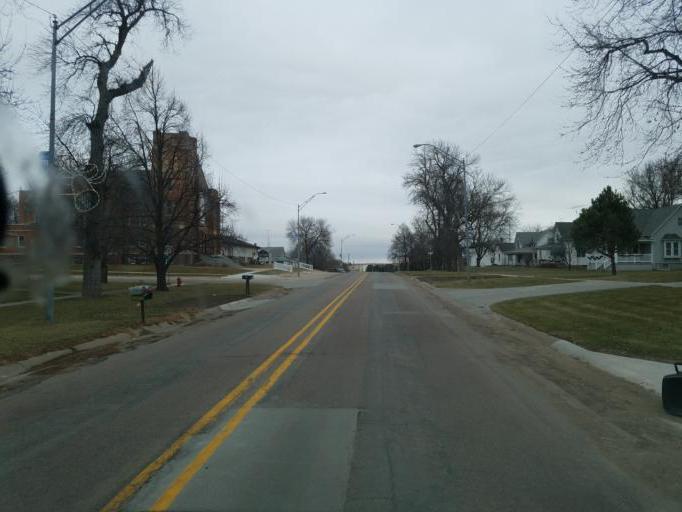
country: US
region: Nebraska
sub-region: Knox County
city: Bloomfield
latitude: 42.5984
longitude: -97.6420
